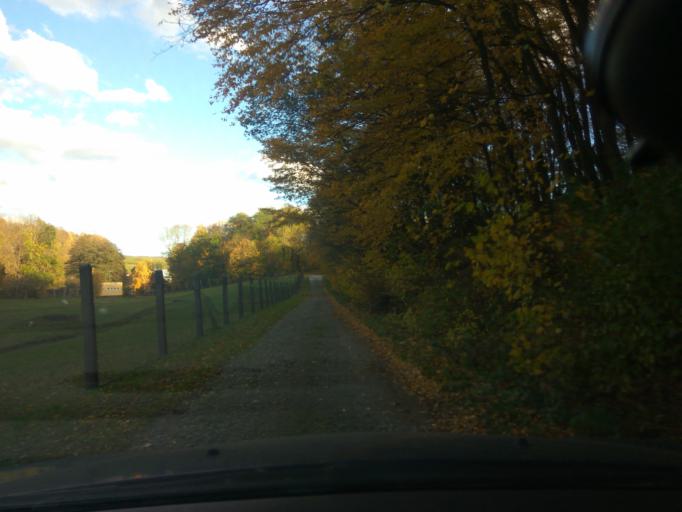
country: SK
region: Nitriansky
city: Brezova pod Bradlom
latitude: 48.6405
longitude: 17.6252
